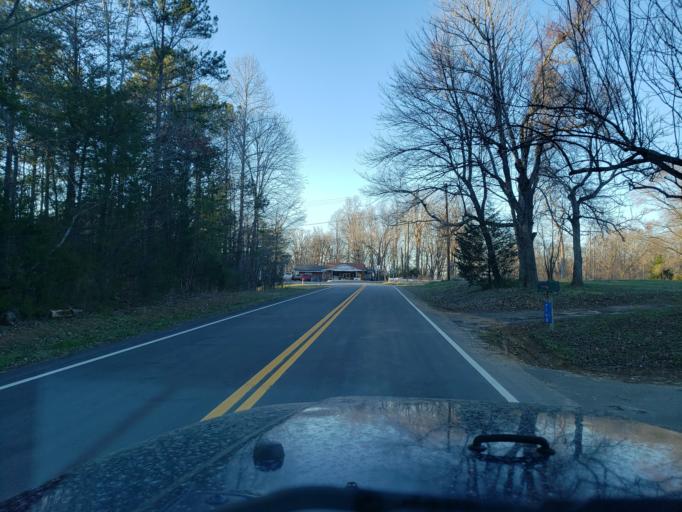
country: US
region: South Carolina
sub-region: Cherokee County
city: Blacksburg
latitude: 35.0421
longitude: -81.4057
